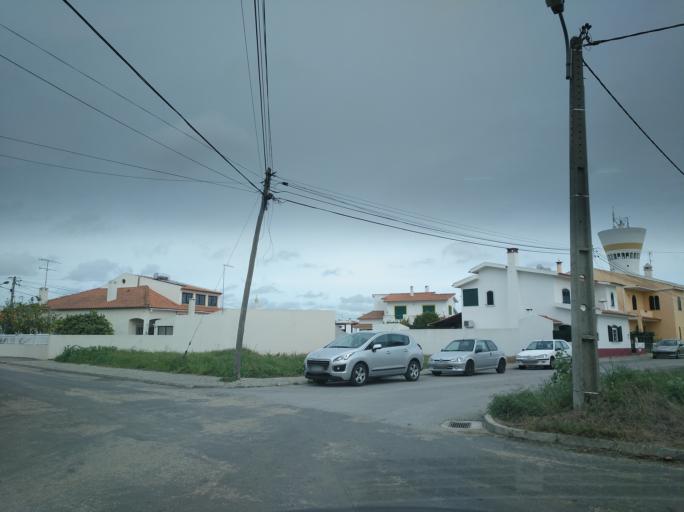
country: PT
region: Setubal
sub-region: Grandola
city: Grandola
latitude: 38.1827
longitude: -8.5701
